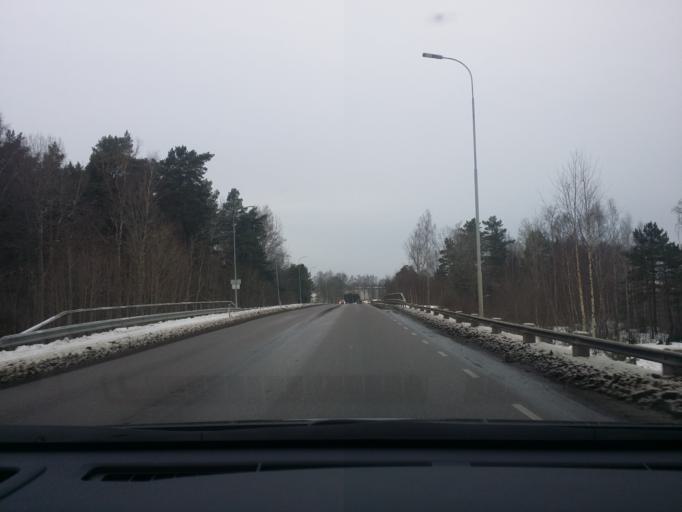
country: SE
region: Vaestra Goetaland
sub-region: Mariestads Kommun
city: Mariestad
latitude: 58.6902
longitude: 13.8181
